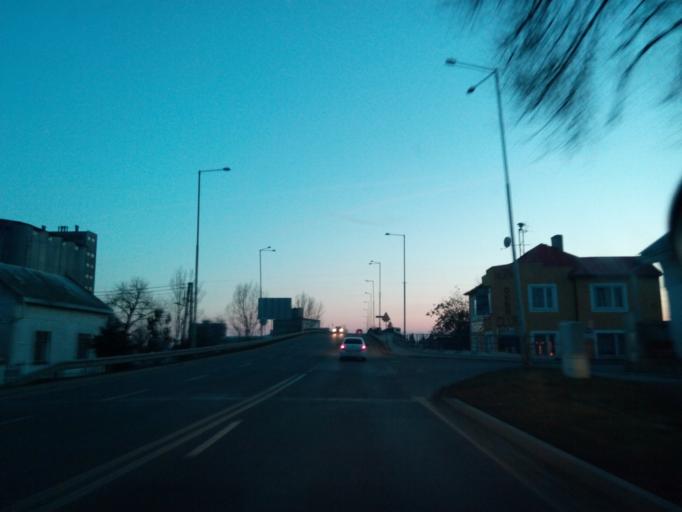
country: SK
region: Kosicky
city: Michalovce
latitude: 48.7484
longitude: 21.9044
